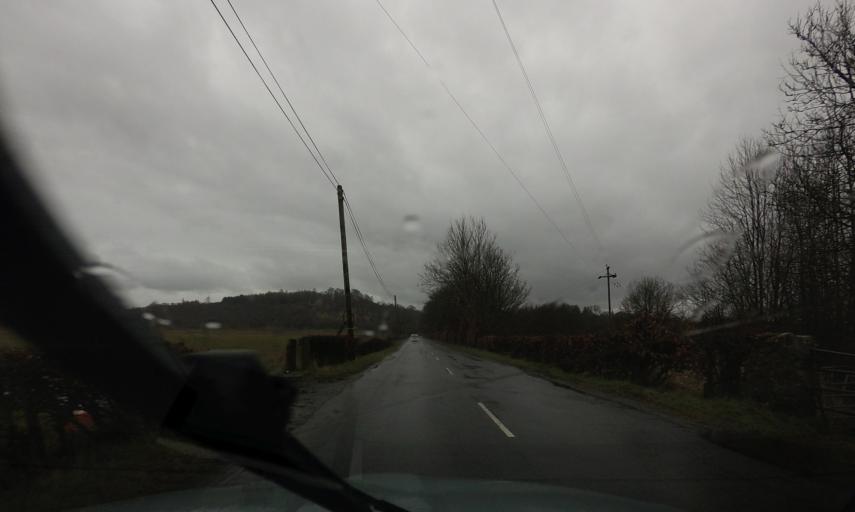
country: GB
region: Scotland
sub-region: Stirling
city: Balfron
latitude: 56.1502
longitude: -4.3609
